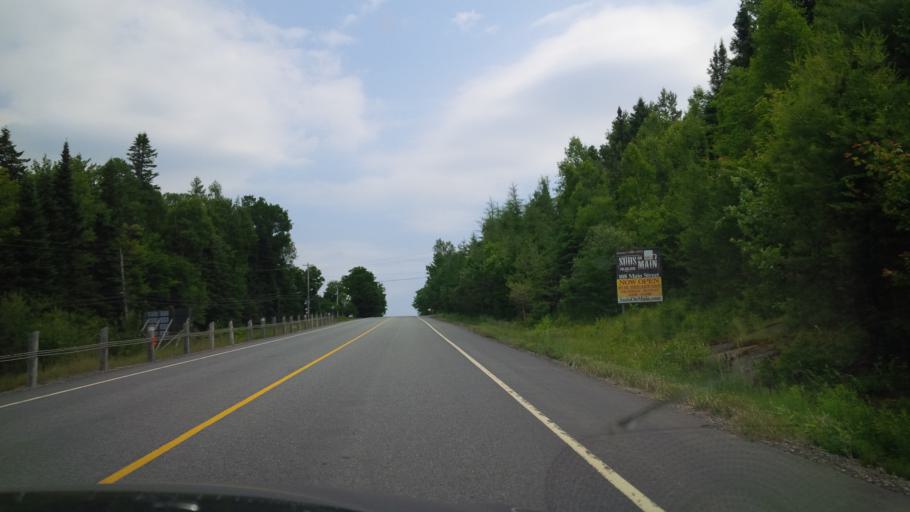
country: CA
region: Ontario
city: Huntsville
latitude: 45.5364
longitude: -79.2901
